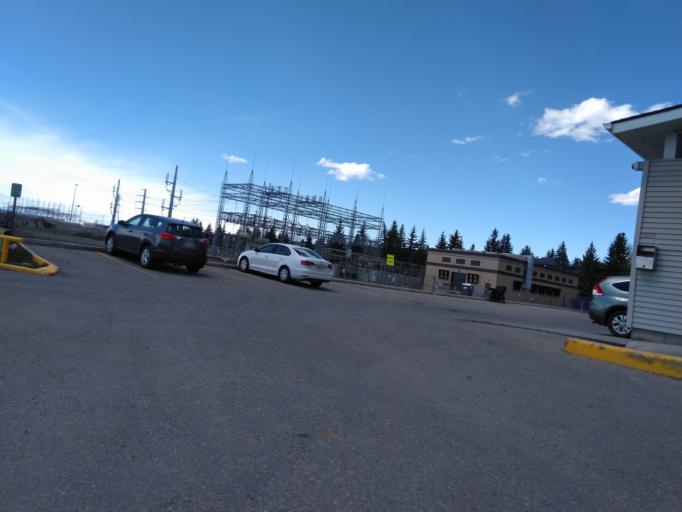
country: CA
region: Alberta
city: Calgary
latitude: 51.0095
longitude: -114.1595
